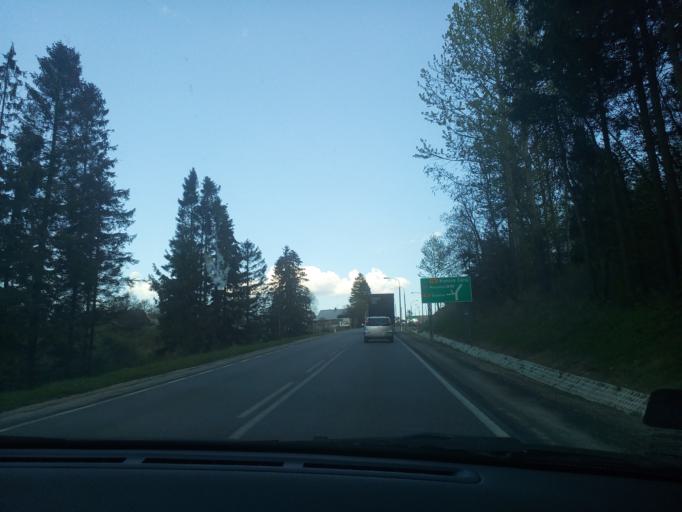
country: PL
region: Lesser Poland Voivodeship
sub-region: Powiat nowosadecki
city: Krynica-Zdroj
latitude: 49.4647
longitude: 20.9509
